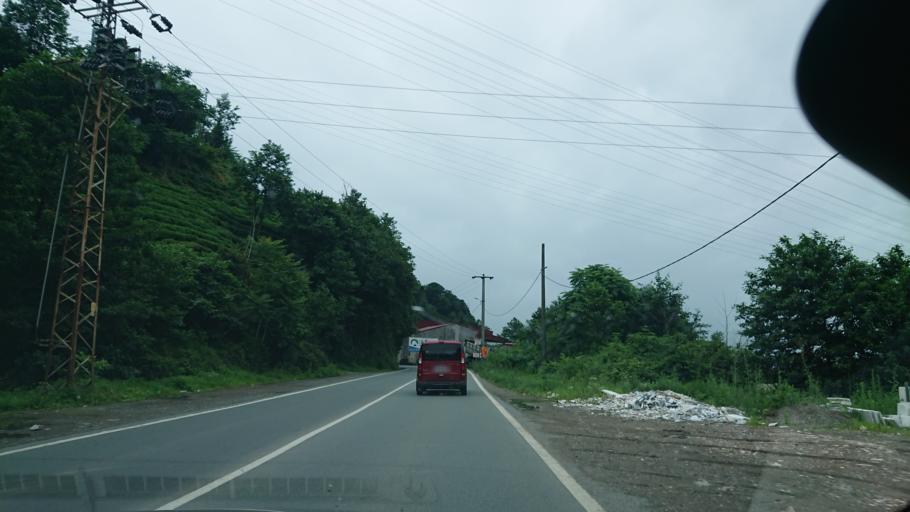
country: TR
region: Rize
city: Gundogdu
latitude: 41.0329
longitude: 40.5816
